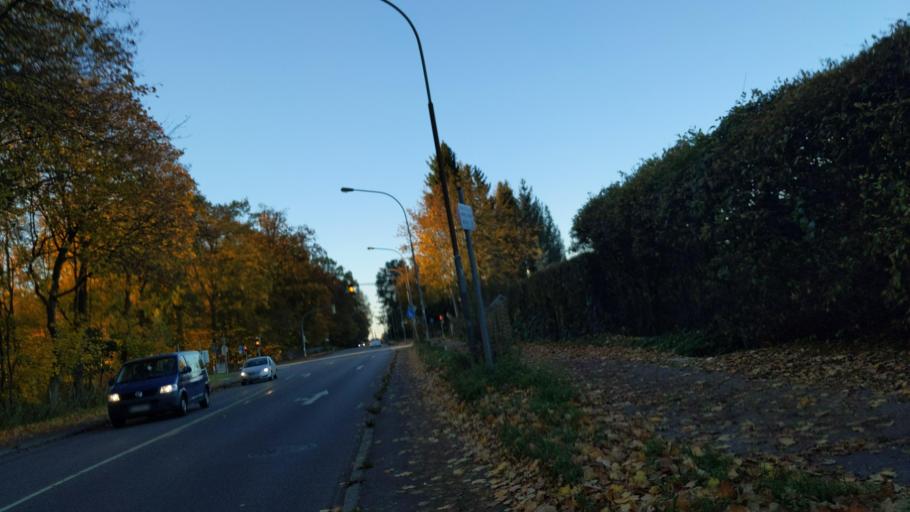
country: DE
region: Schleswig-Holstein
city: Luebeck
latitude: 53.8362
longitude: 10.7129
